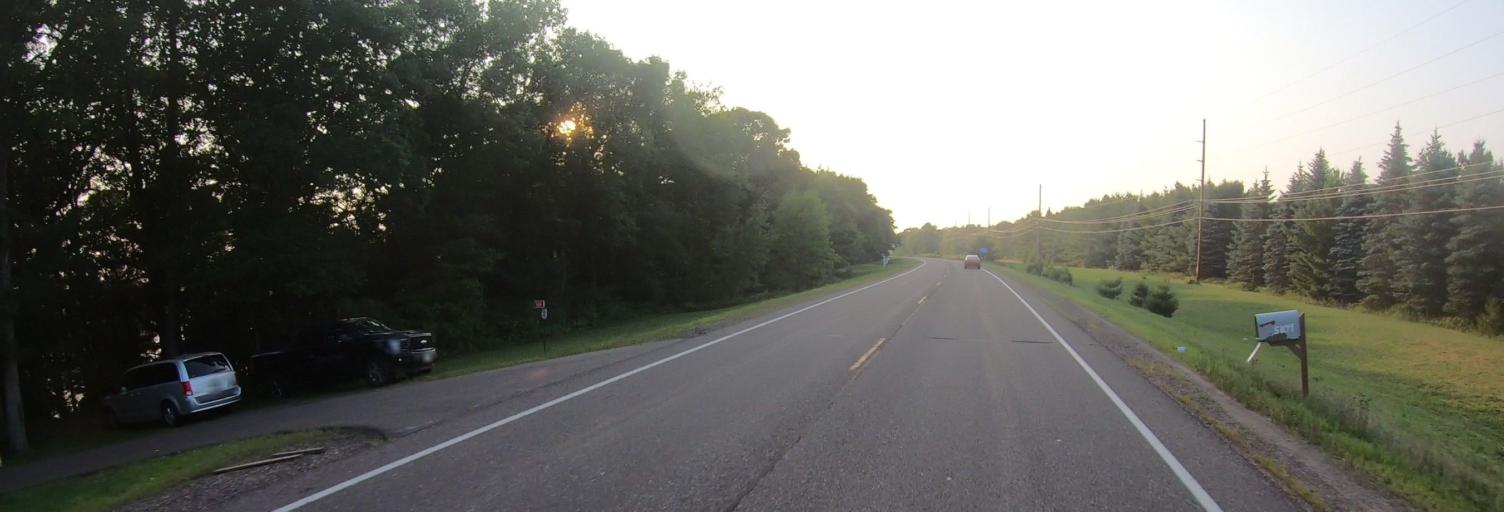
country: US
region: Wisconsin
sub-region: Burnett County
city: Siren
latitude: 45.8191
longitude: -92.2424
